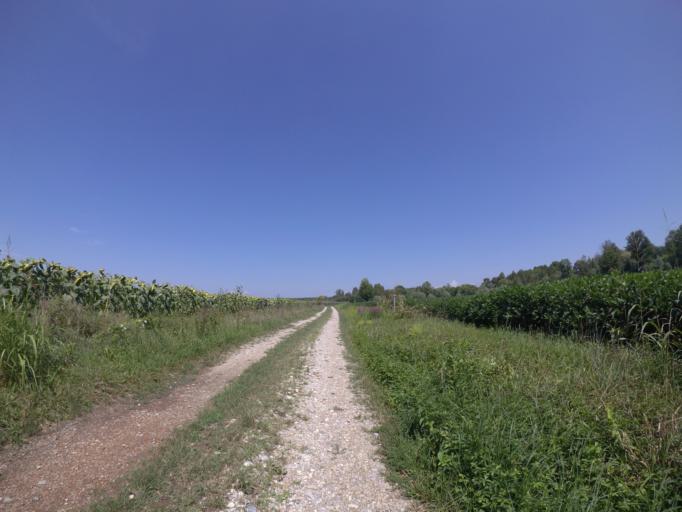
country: IT
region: Friuli Venezia Giulia
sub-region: Provincia di Udine
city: Varmo
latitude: 45.9054
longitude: 13.0156
